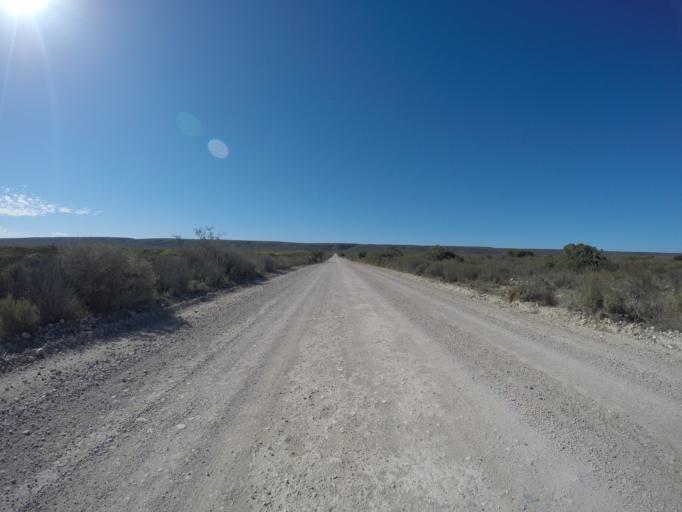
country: ZA
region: Western Cape
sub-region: Overberg District Municipality
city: Bredasdorp
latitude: -34.4442
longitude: 20.4218
